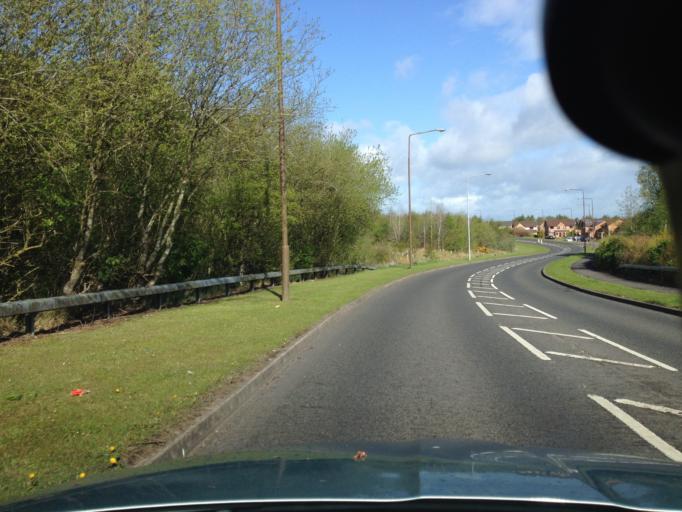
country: GB
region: Scotland
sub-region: West Lothian
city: Livingston
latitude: 55.8700
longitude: -3.5156
